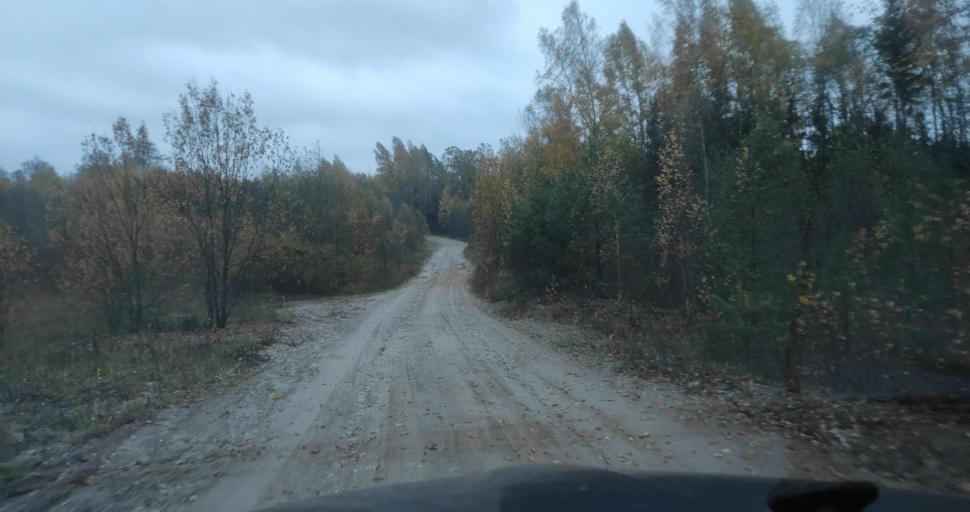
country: LV
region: Kuldigas Rajons
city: Kuldiga
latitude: 56.9066
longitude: 21.9268
